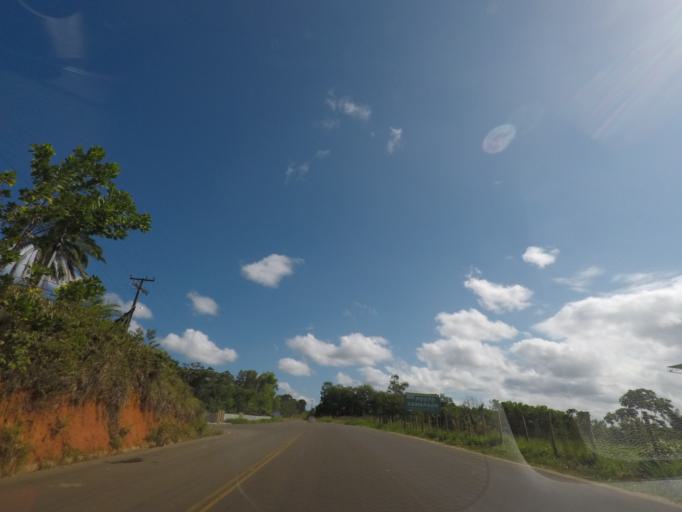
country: BR
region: Bahia
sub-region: Camamu
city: Camamu
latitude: -13.9525
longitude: -39.1073
